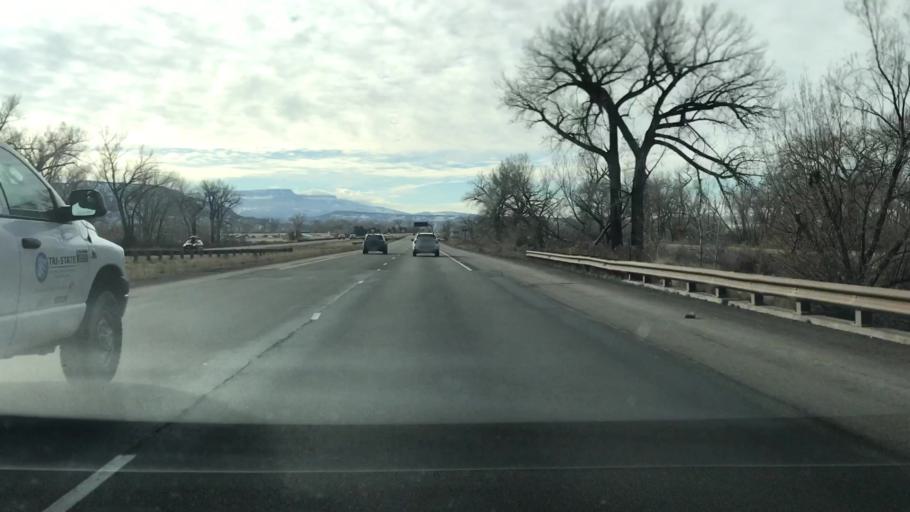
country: US
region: Colorado
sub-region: Garfield County
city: Parachute
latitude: 39.3416
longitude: -108.1928
